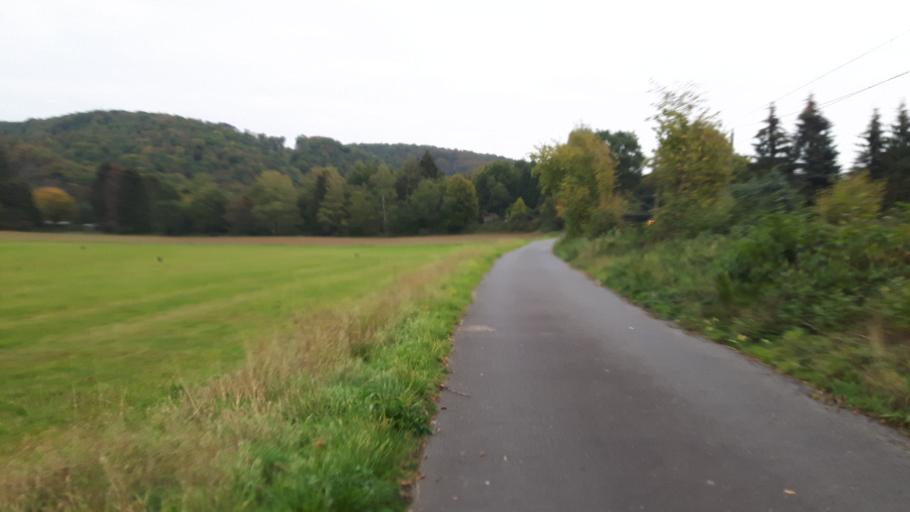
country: DE
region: North Rhine-Westphalia
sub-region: Regierungsbezirk Koln
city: Eitorf
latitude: 50.7753
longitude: 7.3734
